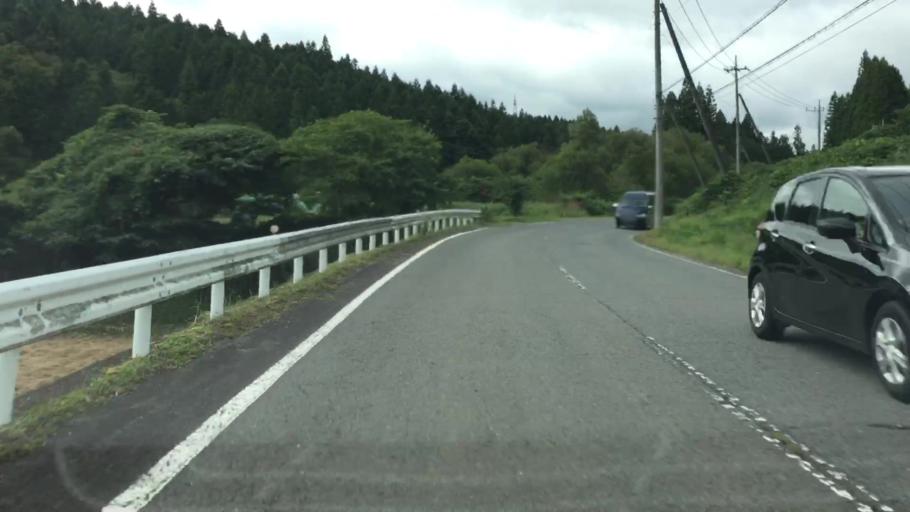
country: JP
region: Tochigi
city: Nikko
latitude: 36.7508
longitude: 139.6586
